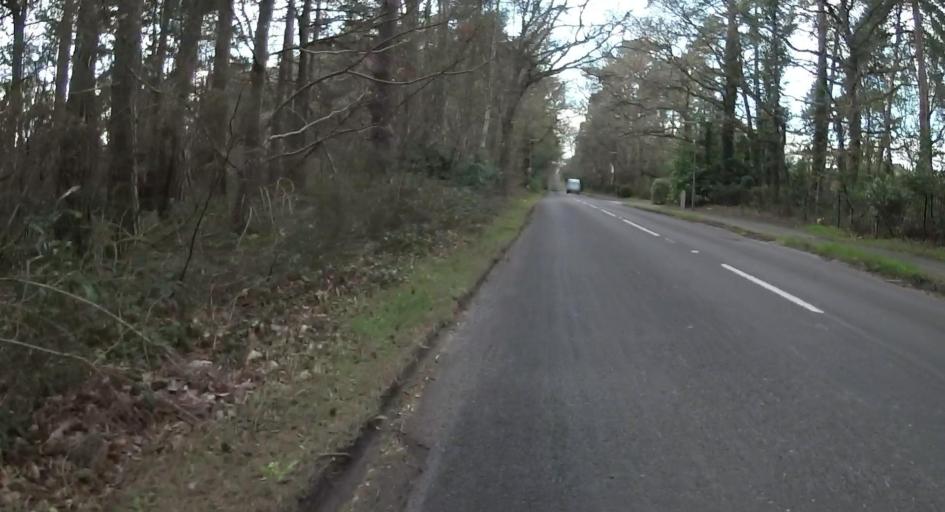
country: GB
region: England
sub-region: Surrey
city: Bagshot
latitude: 51.3223
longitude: -0.7001
